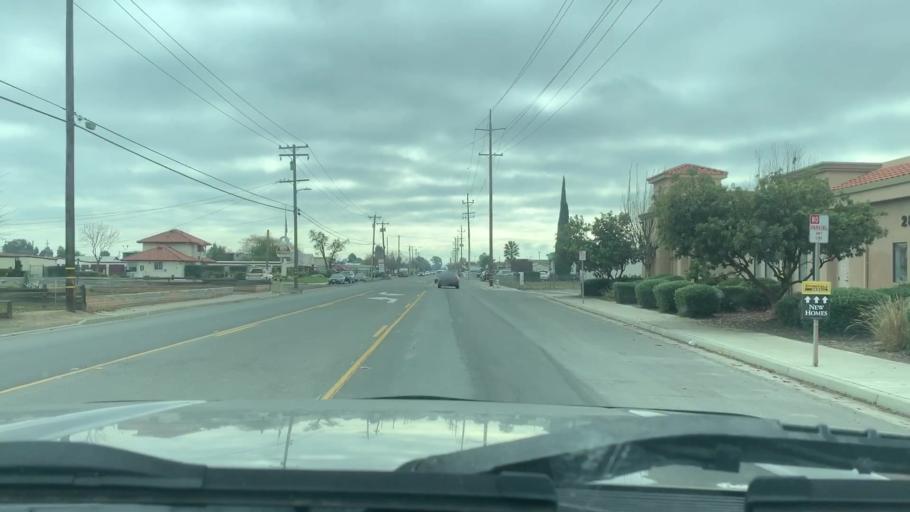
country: US
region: California
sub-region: Merced County
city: Los Banos
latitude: 37.0654
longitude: -120.8353
